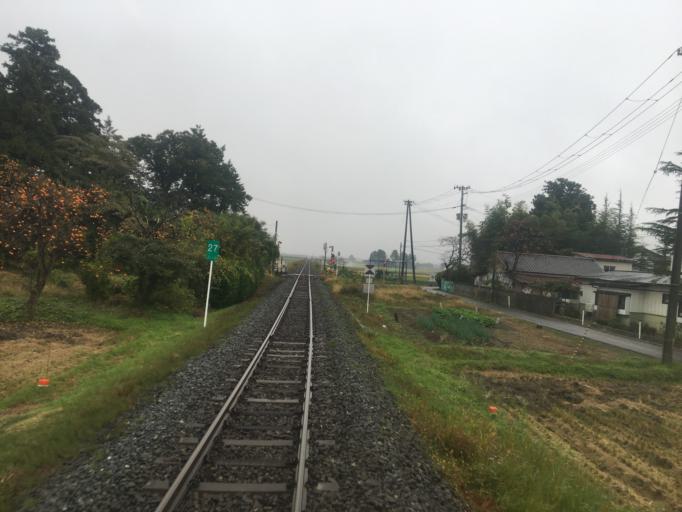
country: JP
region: Miyagi
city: Furukawa
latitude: 38.5748
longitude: 140.9005
